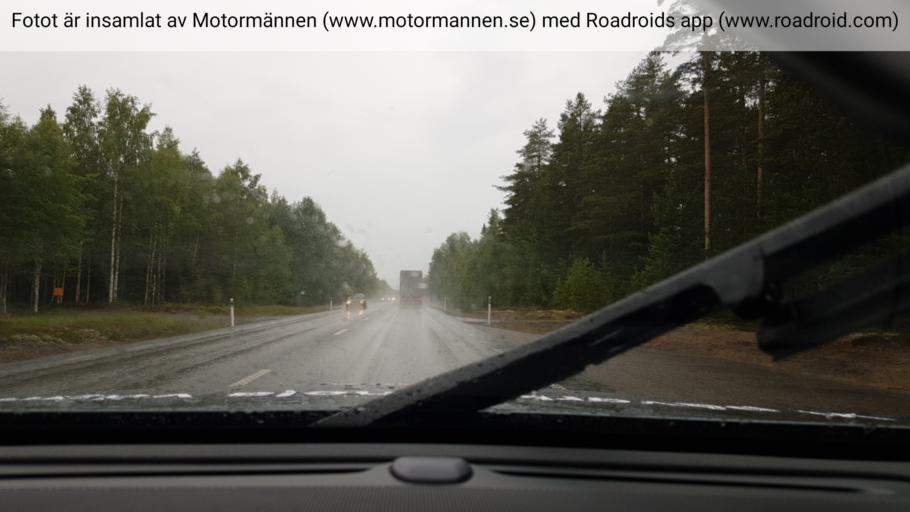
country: SE
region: Vaesterbotten
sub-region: Umea Kommun
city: Roback
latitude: 63.8510
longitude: 20.1154
